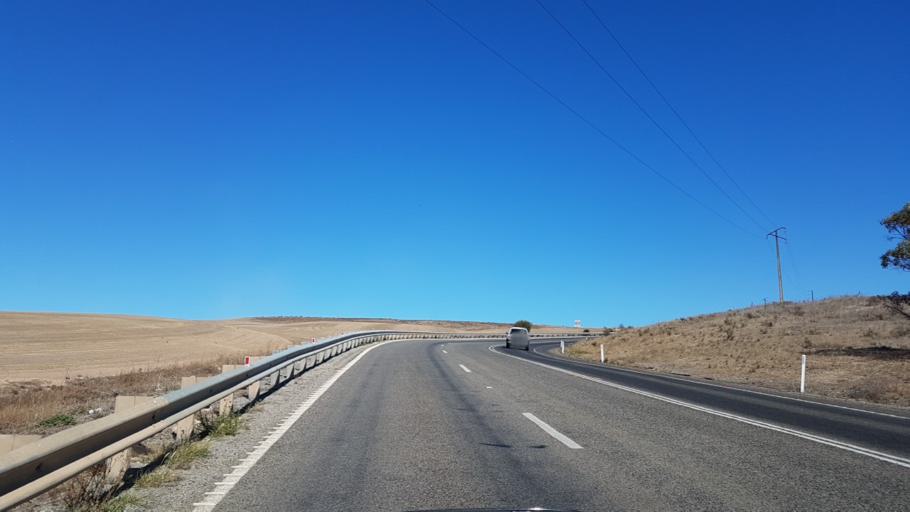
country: AU
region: South Australia
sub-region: Wakefield
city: Balaklava
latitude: -34.0676
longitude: 138.0616
